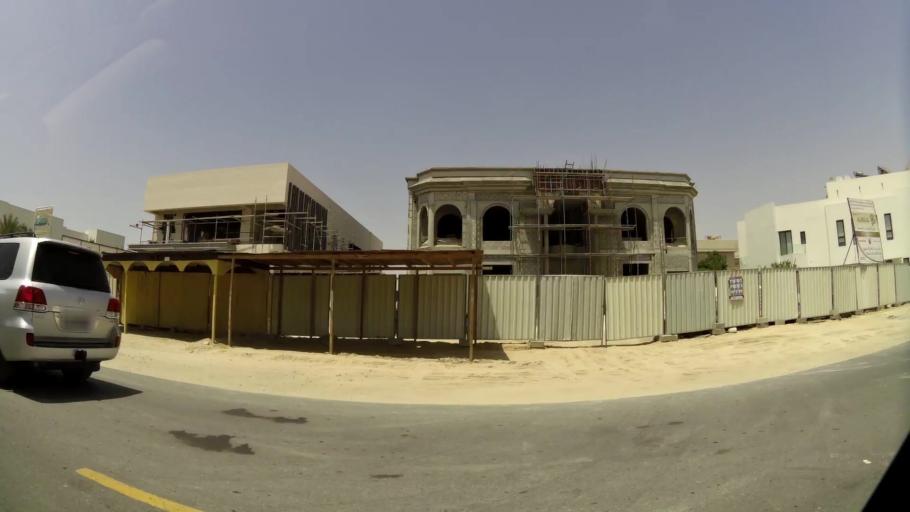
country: AE
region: Dubai
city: Dubai
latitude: 25.1343
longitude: 55.2041
